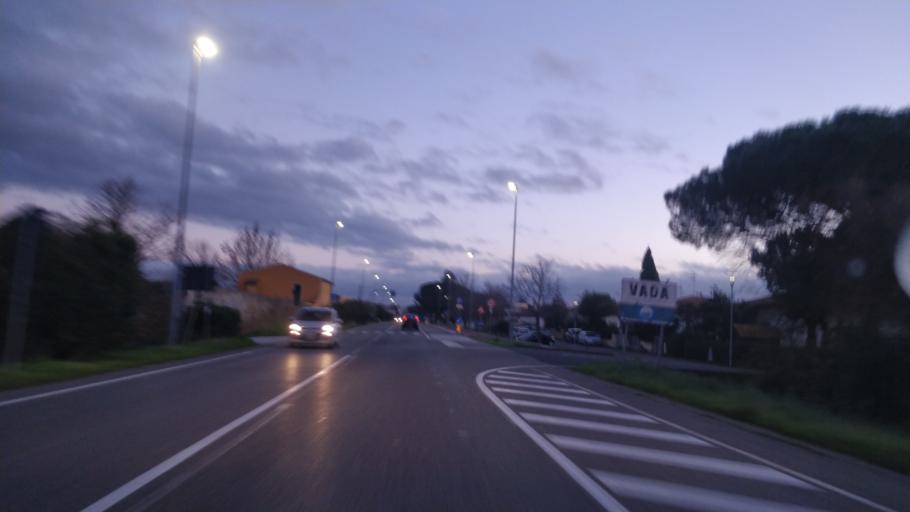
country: IT
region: Tuscany
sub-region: Provincia di Livorno
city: Vada
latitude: 43.3591
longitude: 10.4540
